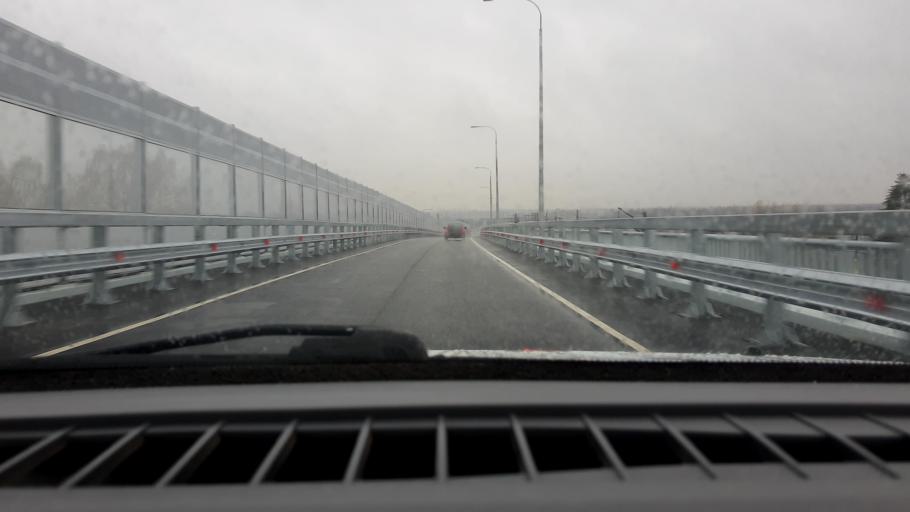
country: RU
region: Nizjnij Novgorod
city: Neklyudovo
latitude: 56.4003
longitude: 43.9822
